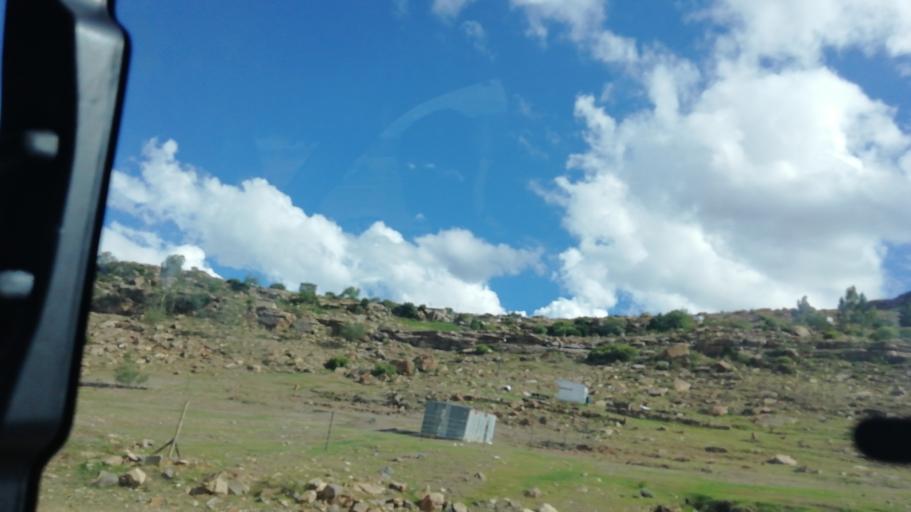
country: LS
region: Maseru
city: Maseru
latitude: -29.4048
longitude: 27.4652
